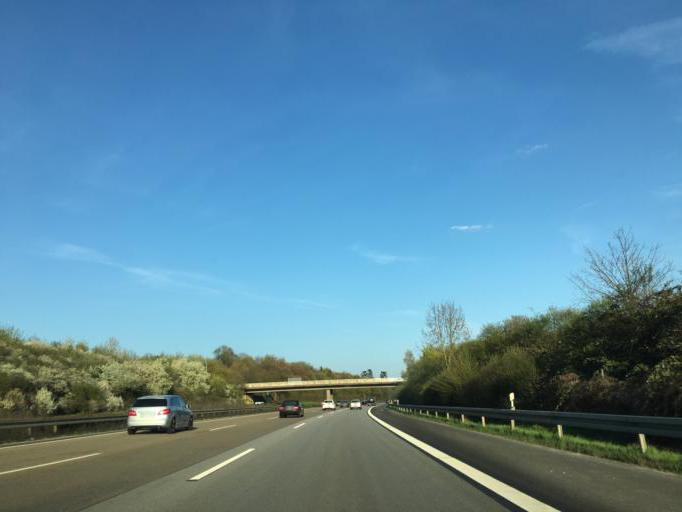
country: DE
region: Hesse
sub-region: Regierungsbezirk Darmstadt
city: Maintal
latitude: 50.1484
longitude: 8.8338
